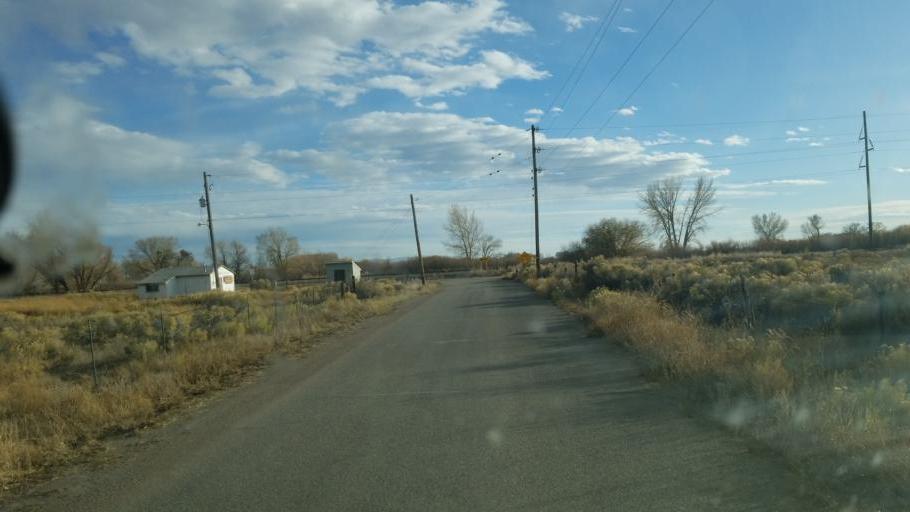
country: US
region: Colorado
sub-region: Alamosa County
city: Alamosa East
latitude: 37.4676
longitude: -105.8480
